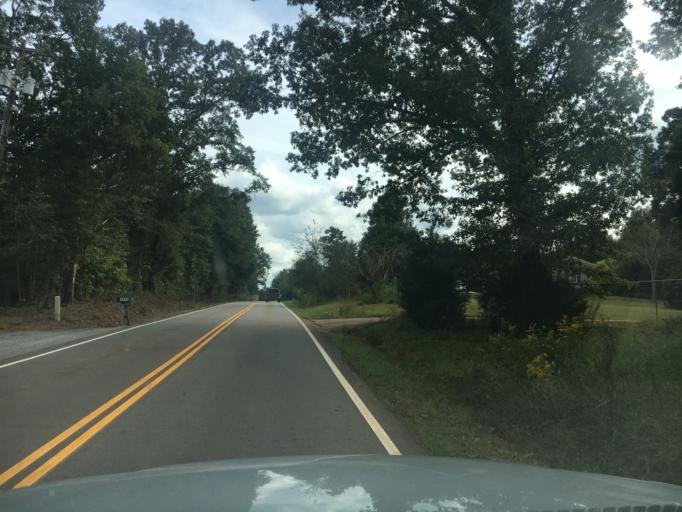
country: US
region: South Carolina
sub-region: Spartanburg County
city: Wellford
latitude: 34.9205
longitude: -82.0616
